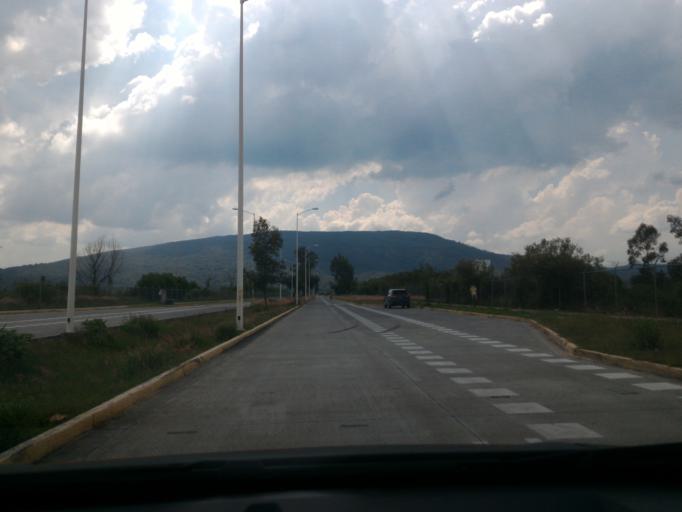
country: MX
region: Jalisco
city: Nuevo Mexico
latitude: 20.6941
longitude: -103.4629
